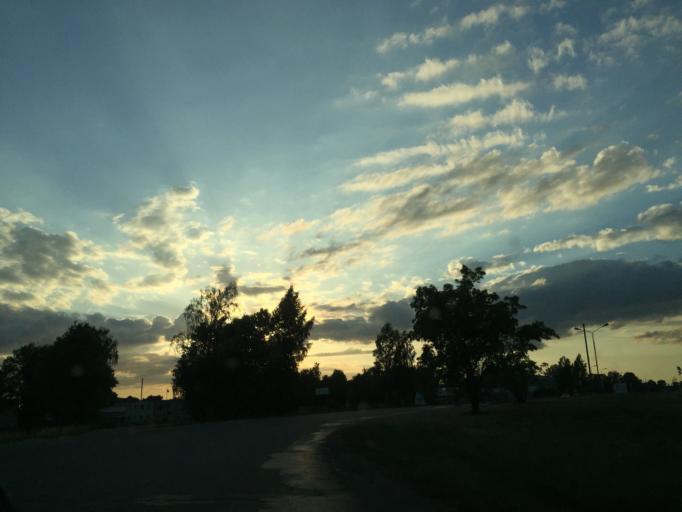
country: LV
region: Sigulda
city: Sigulda
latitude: 57.1415
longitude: 24.8616
